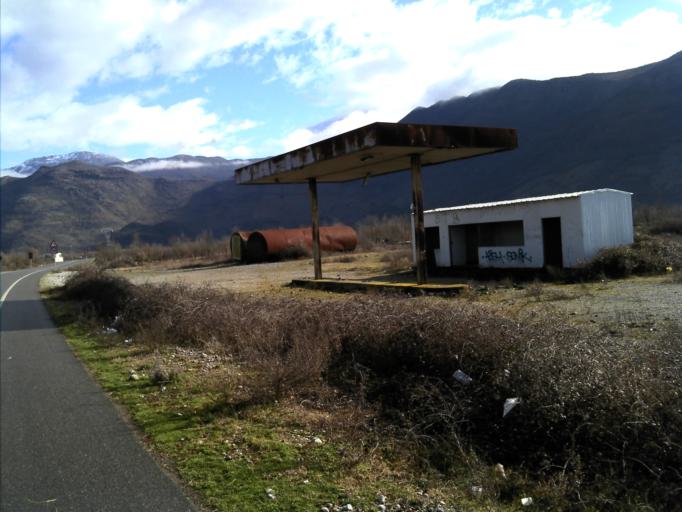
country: AL
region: Shkoder
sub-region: Rrethi i Malesia e Madhe
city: Hot
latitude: 42.2925
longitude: 19.4432
